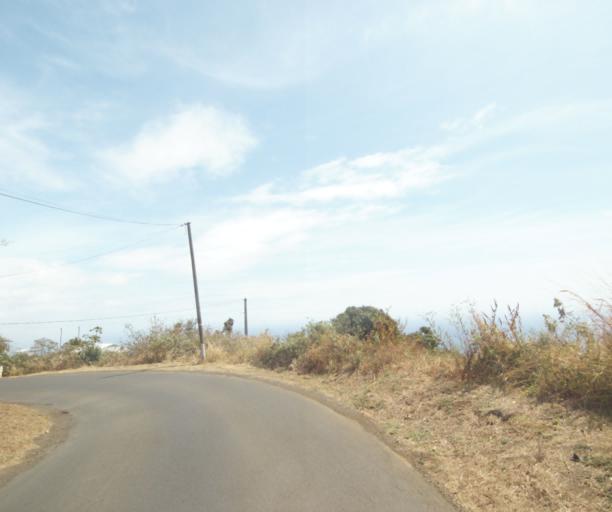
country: RE
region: Reunion
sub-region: Reunion
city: Trois-Bassins
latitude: -21.0965
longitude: 55.2766
